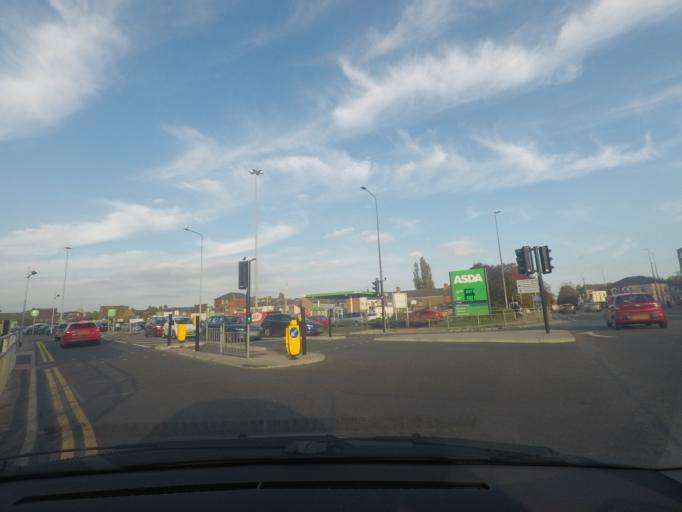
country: GB
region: England
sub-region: North East Lincolnshire
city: Grimsby
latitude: 53.5674
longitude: -0.0761
